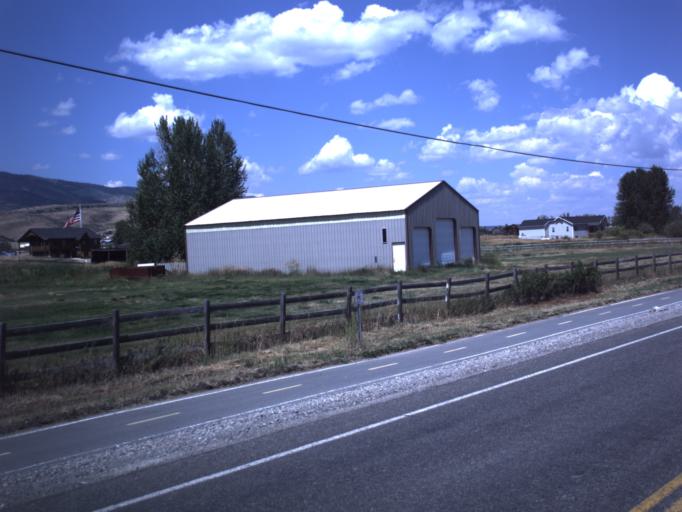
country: US
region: Idaho
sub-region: Bear Lake County
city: Paris
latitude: 41.9335
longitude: -111.3947
